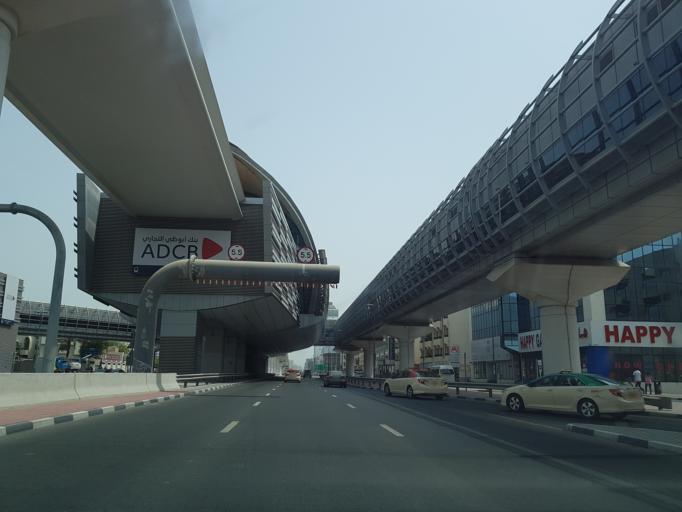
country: AE
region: Ash Shariqah
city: Sharjah
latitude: 25.2435
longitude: 55.2978
